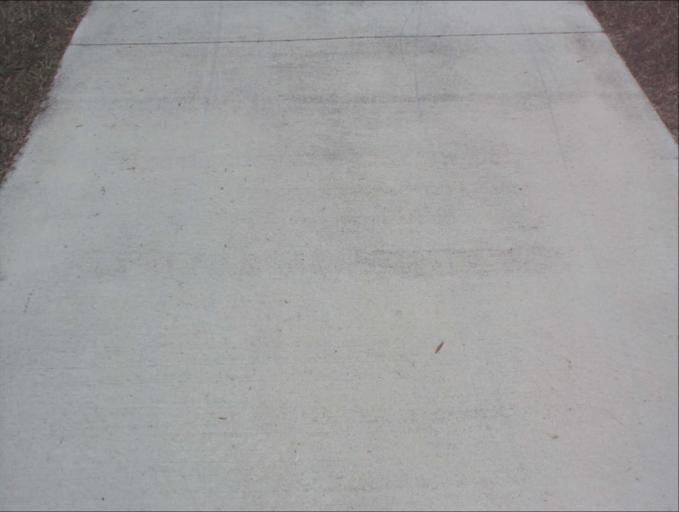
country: AU
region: Queensland
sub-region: Logan
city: Windaroo
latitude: -27.7355
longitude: 153.2067
